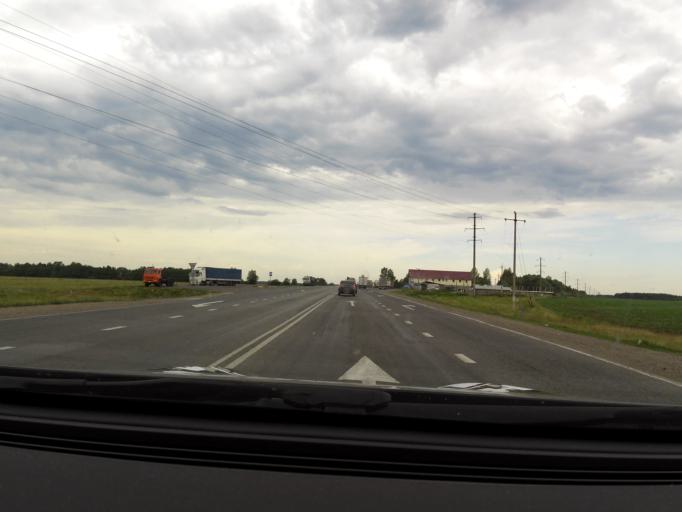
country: RU
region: Bashkortostan
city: Kudeyevskiy
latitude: 54.8168
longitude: 56.7395
